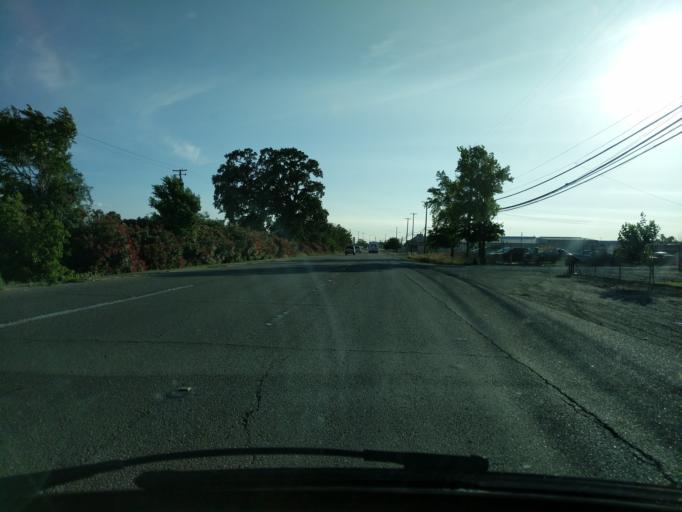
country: US
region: California
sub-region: San Joaquin County
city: Kennedy
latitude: 37.9439
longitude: -121.2603
